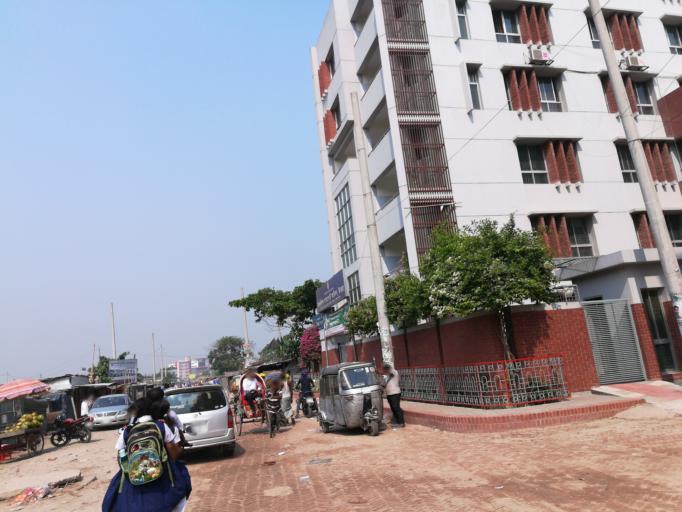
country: BD
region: Dhaka
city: Tungi
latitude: 23.8691
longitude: 90.3789
